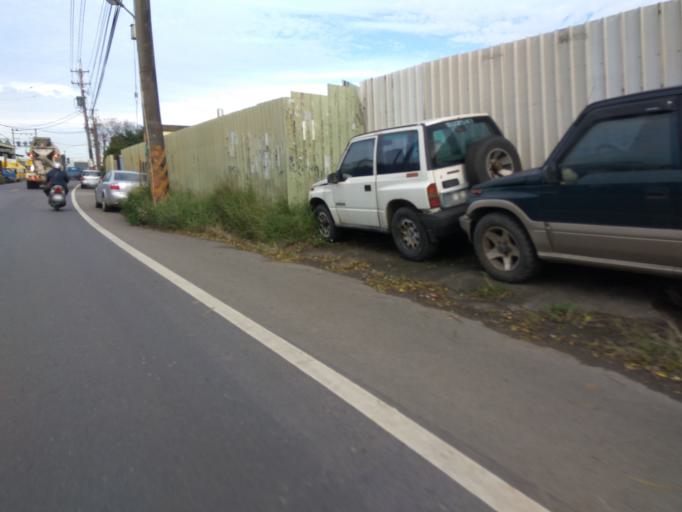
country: TW
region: Taiwan
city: Daxi
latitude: 24.9399
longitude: 121.1596
